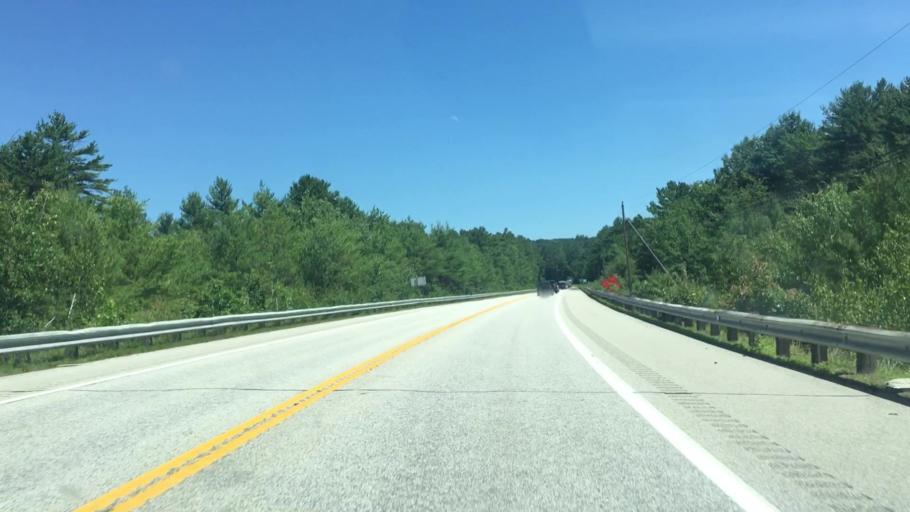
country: US
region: New Hampshire
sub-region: Merrimack County
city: Hopkinton
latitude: 43.1793
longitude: -71.7050
